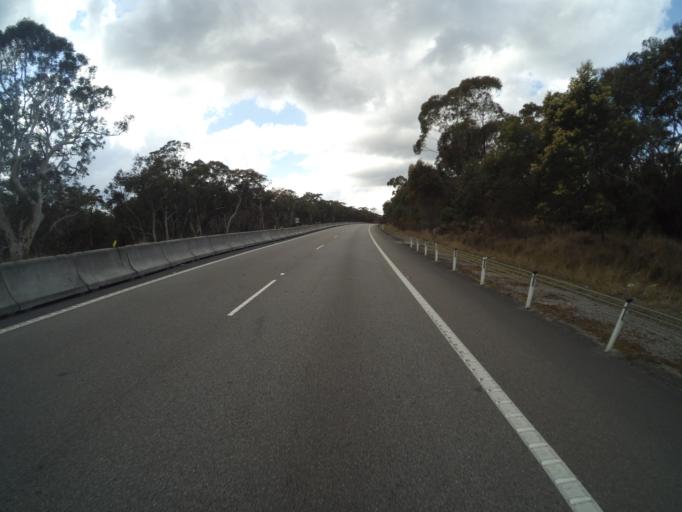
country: AU
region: New South Wales
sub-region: Wollongong
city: Mount Keira
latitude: -34.3216
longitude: 150.7645
